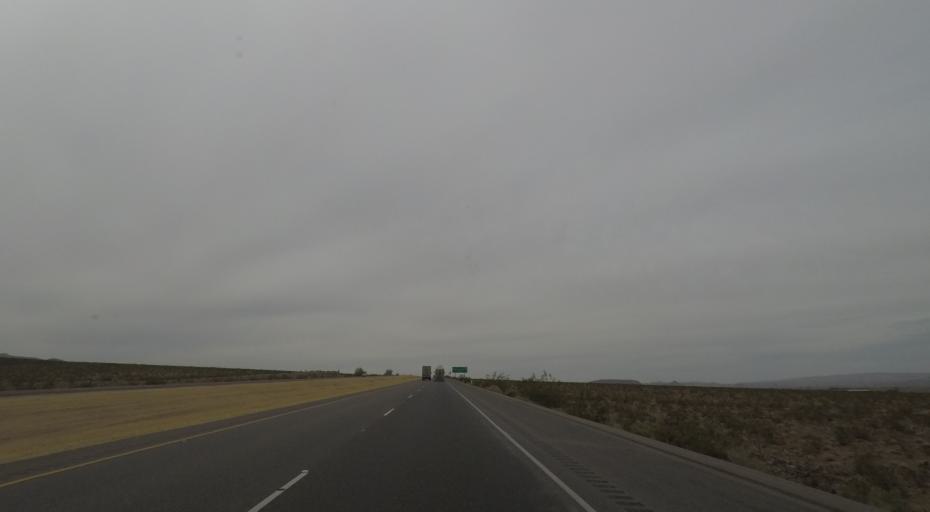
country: US
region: California
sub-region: San Bernardino County
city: Barstow
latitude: 34.8392
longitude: -116.7866
